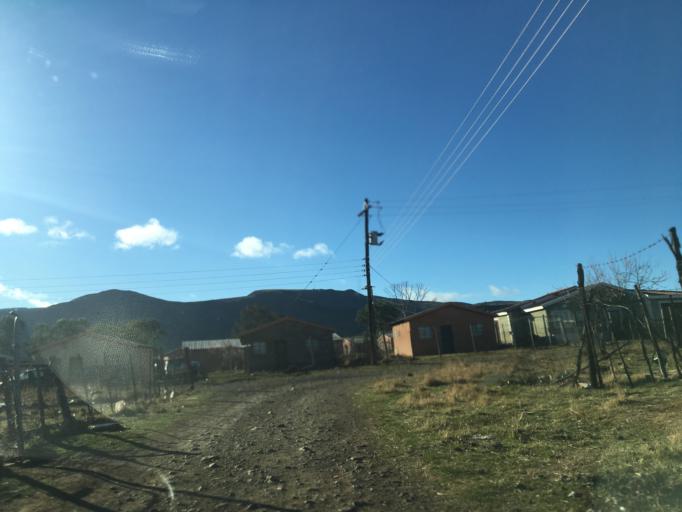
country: ZA
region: Eastern Cape
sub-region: Chris Hani District Municipality
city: Cala
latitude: -31.5410
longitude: 27.6861
